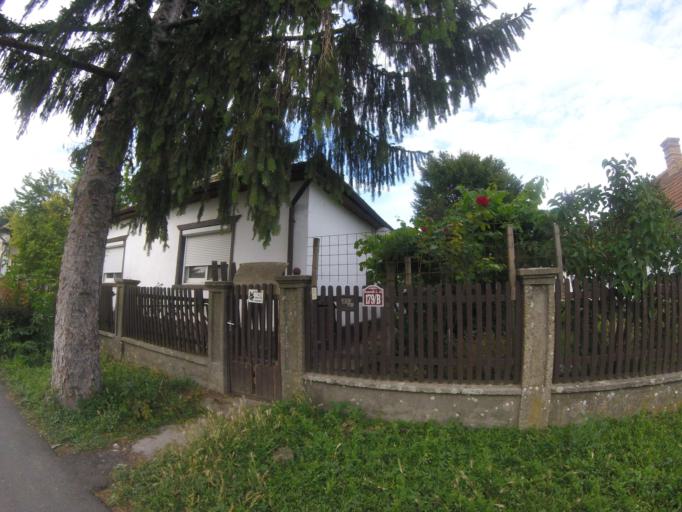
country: HU
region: Heves
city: Tiszanana
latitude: 47.5968
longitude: 20.5879
